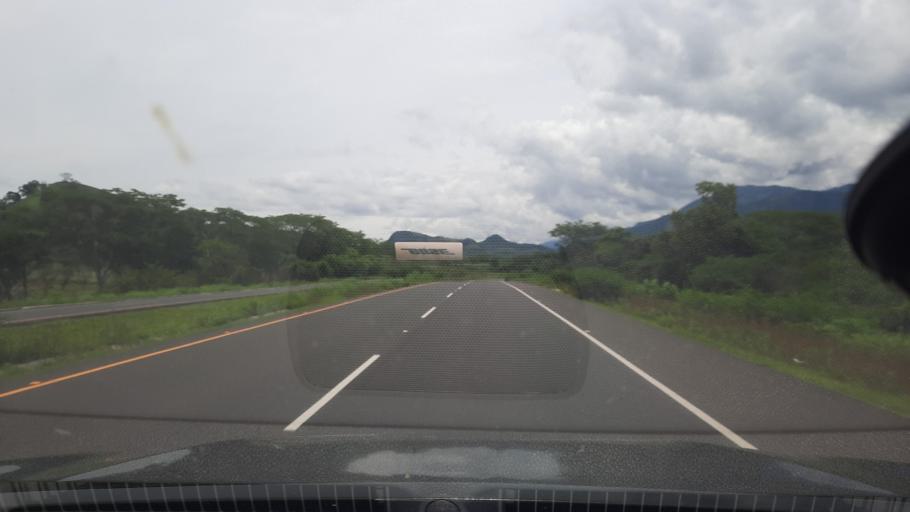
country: HN
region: Valle
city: Aramecina
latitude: 13.7647
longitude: -87.7072
